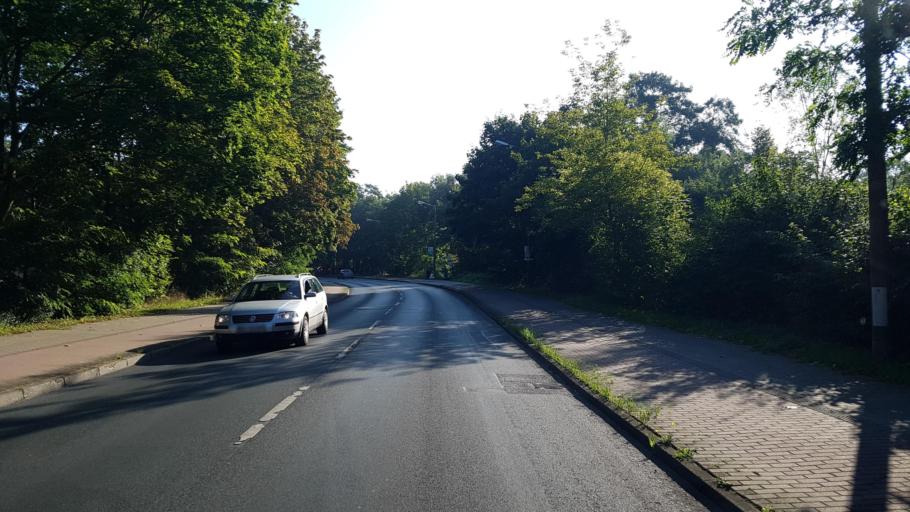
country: DE
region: Brandenburg
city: Brandenburg an der Havel
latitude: 52.4196
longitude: 12.5733
